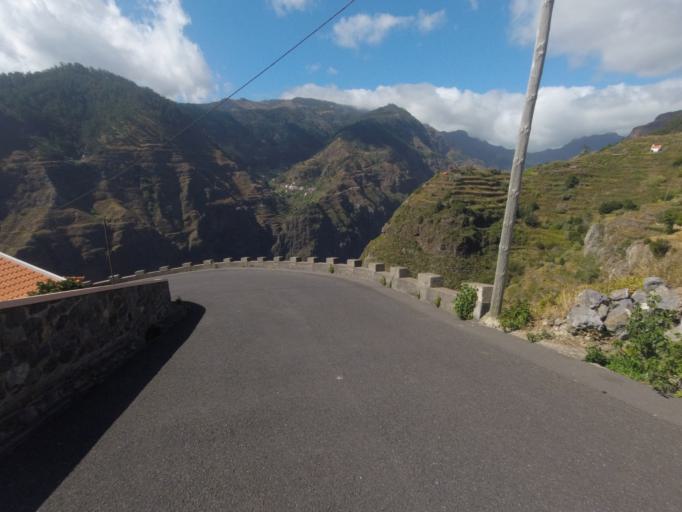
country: PT
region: Madeira
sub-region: Ribeira Brava
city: Campanario
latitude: 32.6932
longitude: -17.0394
